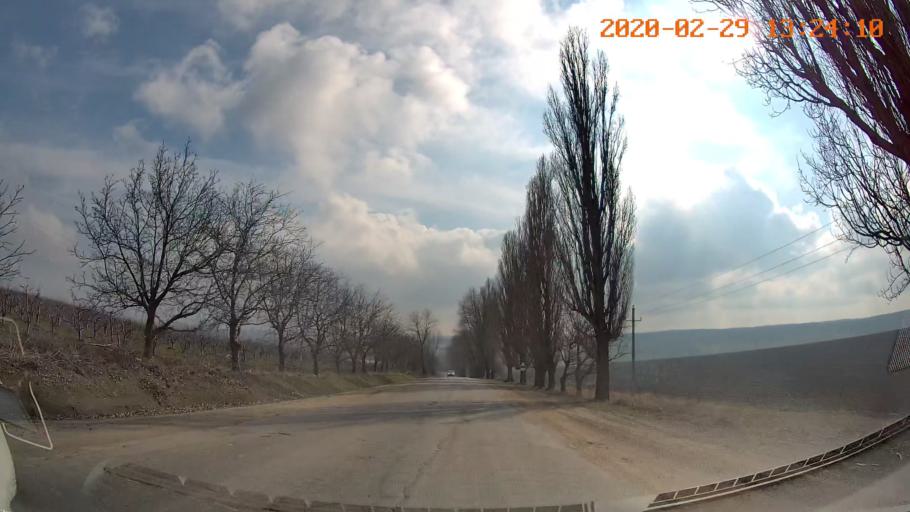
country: MD
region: Telenesti
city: Camenca
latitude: 47.9418
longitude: 28.6261
